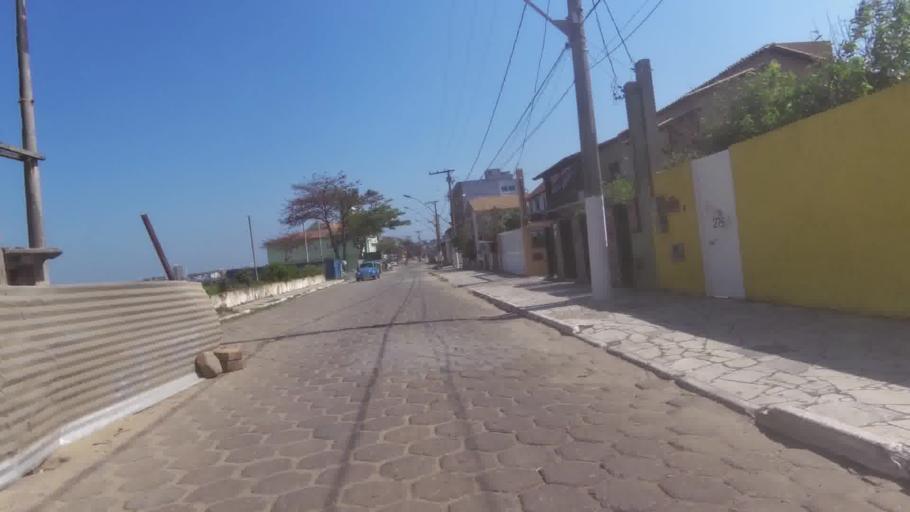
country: BR
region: Espirito Santo
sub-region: Marataizes
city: Marataizes
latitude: -21.0427
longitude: -40.8233
